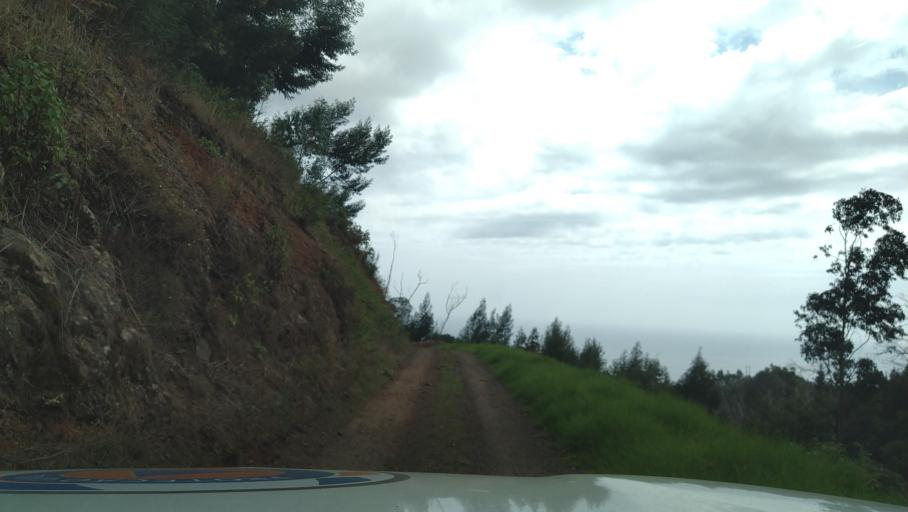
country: PT
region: Madeira
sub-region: Funchal
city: Nossa Senhora do Monte
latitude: 32.6833
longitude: -16.9250
